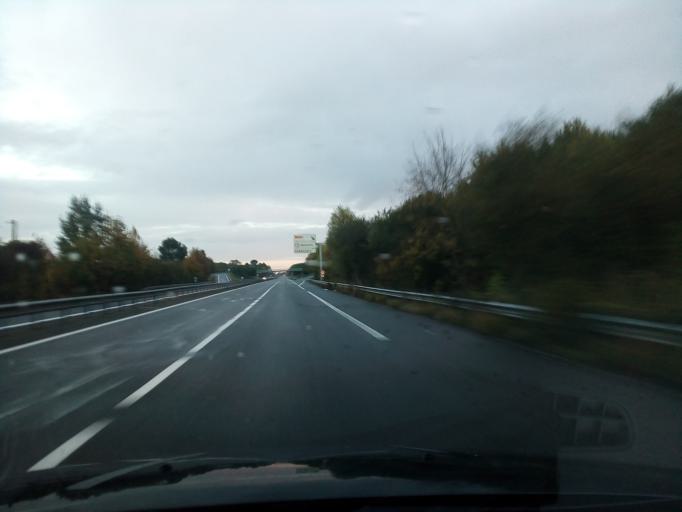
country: FR
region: Aquitaine
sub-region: Departement de la Gironde
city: Gauriaguet
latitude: 45.0633
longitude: -0.3953
